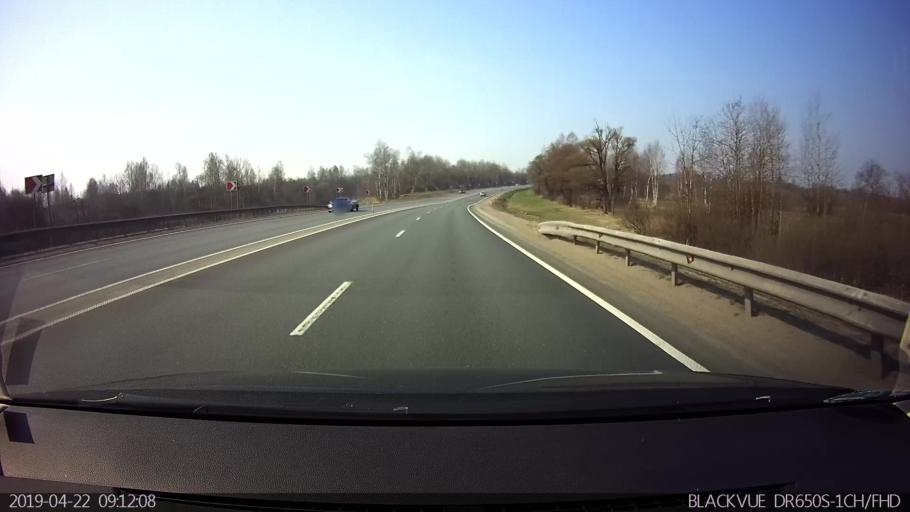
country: RU
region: Smolensk
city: Katyn'
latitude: 54.8153
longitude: 31.6397
